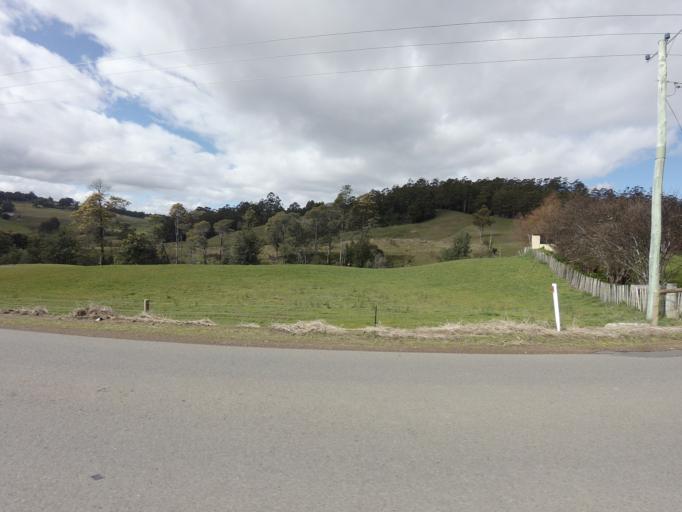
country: AU
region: Tasmania
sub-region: Huon Valley
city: Geeveston
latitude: -43.2468
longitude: 146.9906
